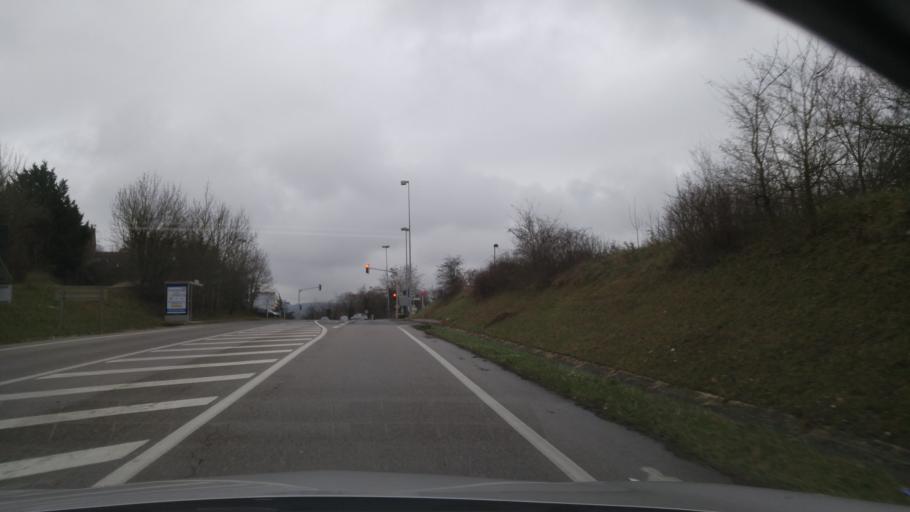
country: FR
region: Rhone-Alpes
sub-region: Departement de l'Isere
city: La Verpilliere
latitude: 45.6254
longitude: 5.1391
